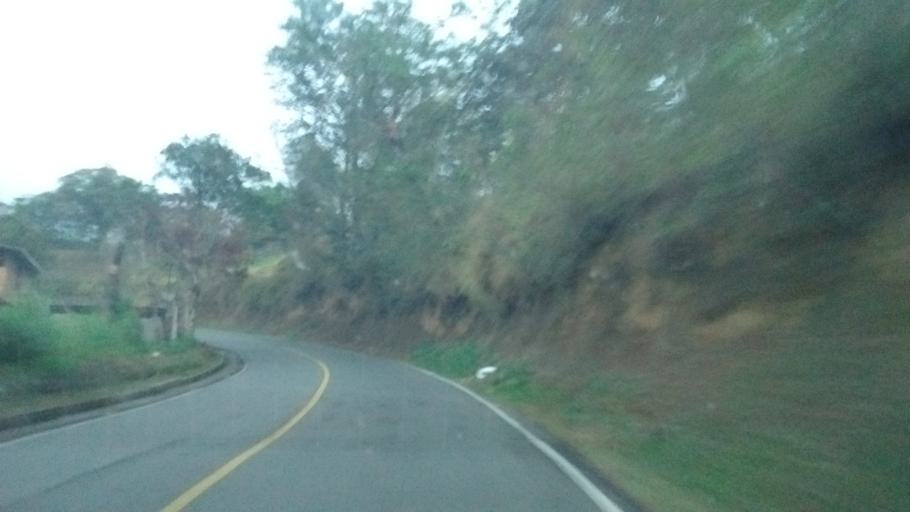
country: CO
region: Cauca
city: Popayan
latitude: 2.3612
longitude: -76.6846
